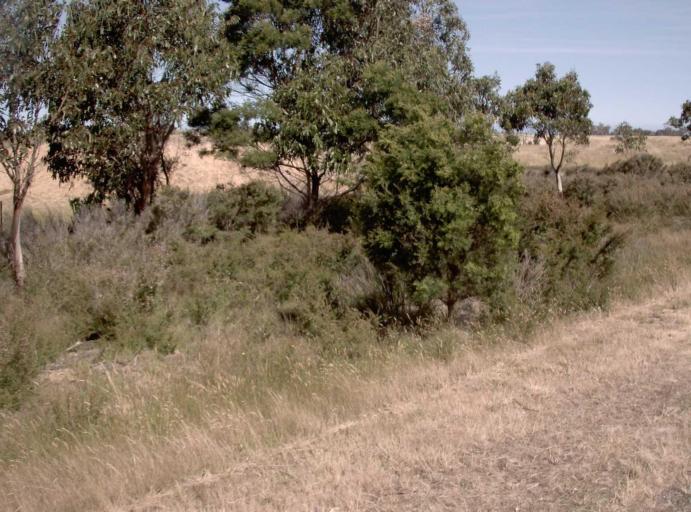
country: AU
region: Victoria
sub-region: Wellington
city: Sale
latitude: -38.3320
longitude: 147.1630
